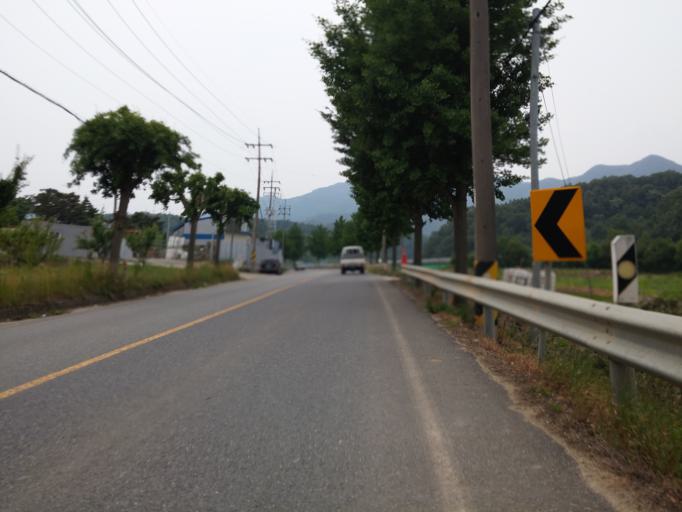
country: KR
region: Chungcheongbuk-do
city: Okcheon
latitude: 36.3002
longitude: 127.5375
